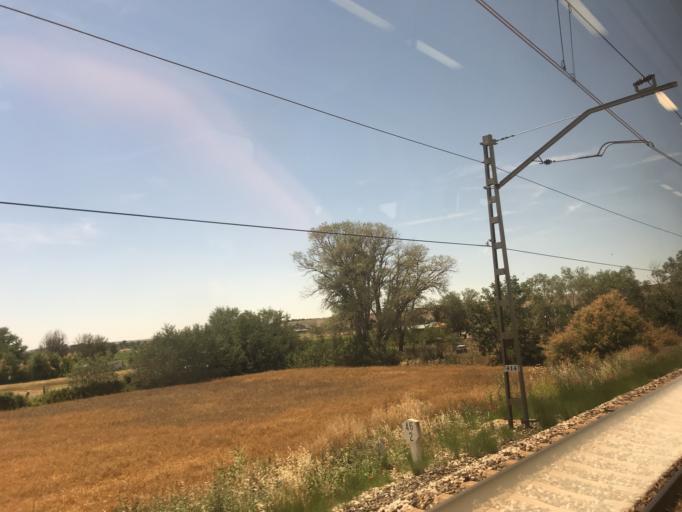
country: ES
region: Madrid
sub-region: Provincia de Madrid
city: Aranjuez
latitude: 40.0506
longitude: -3.6288
